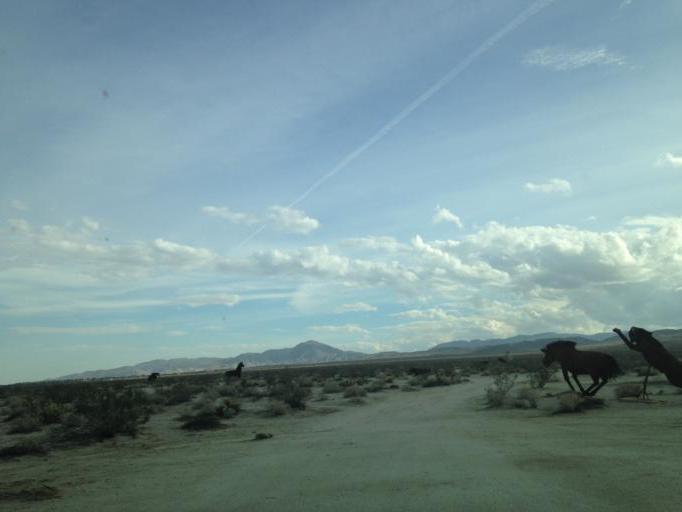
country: US
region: California
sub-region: San Diego County
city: Borrego Springs
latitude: 33.2107
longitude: -116.3551
